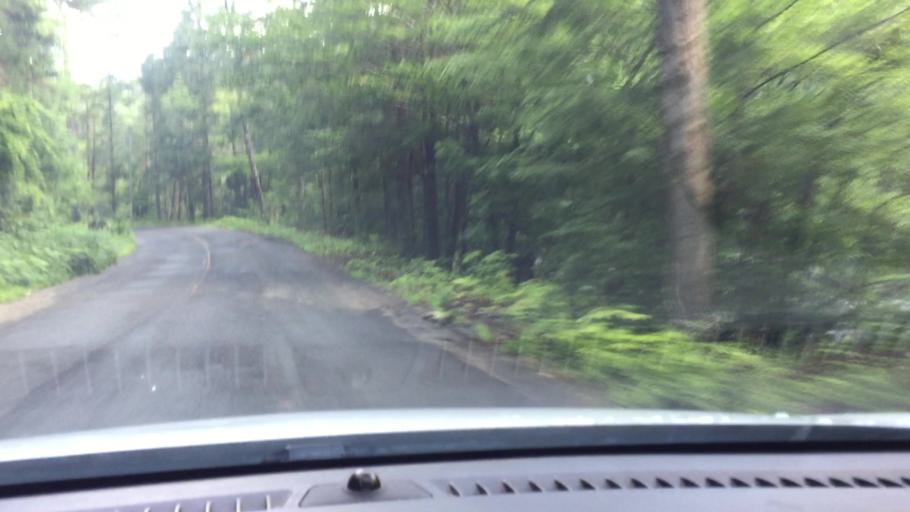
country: US
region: Massachusetts
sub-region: Hampshire County
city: Chesterfield
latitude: 42.3090
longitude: -72.9124
